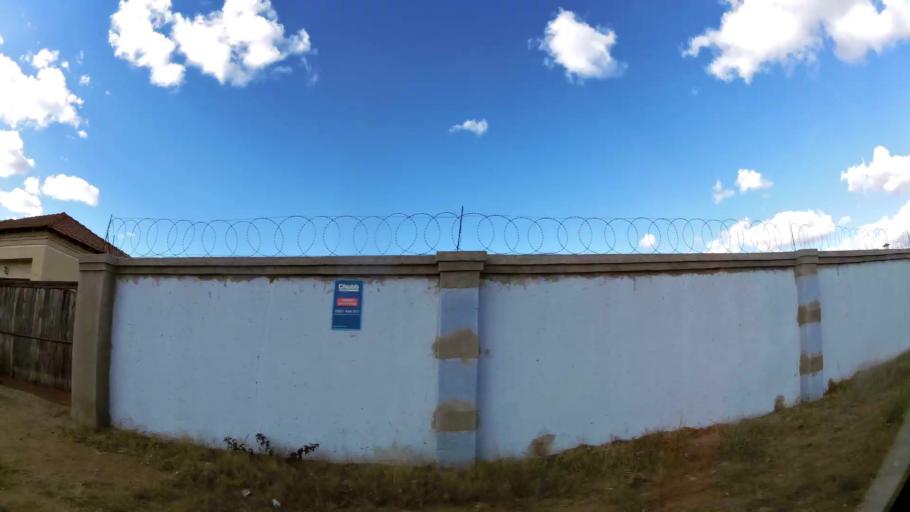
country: ZA
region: Limpopo
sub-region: Capricorn District Municipality
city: Polokwane
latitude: -23.9157
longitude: 29.5030
